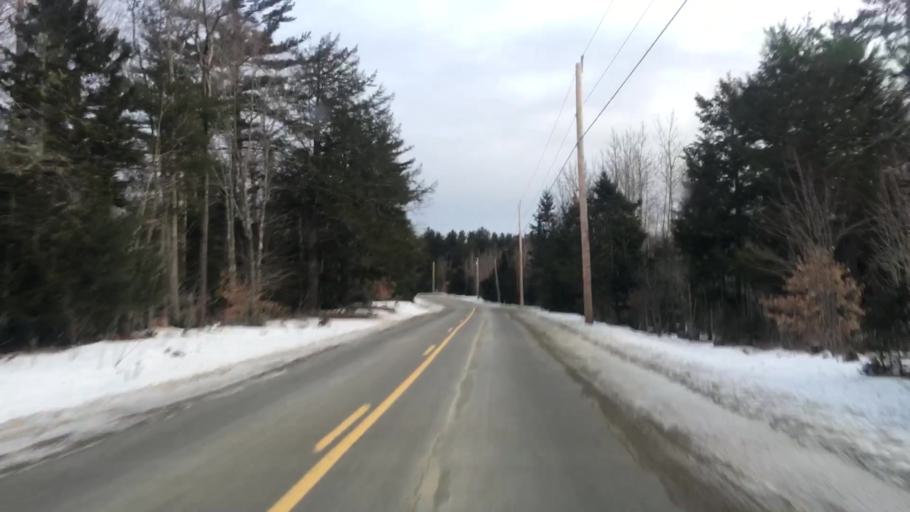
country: US
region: Maine
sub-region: Hancock County
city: Franklin
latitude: 44.7611
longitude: -68.3250
